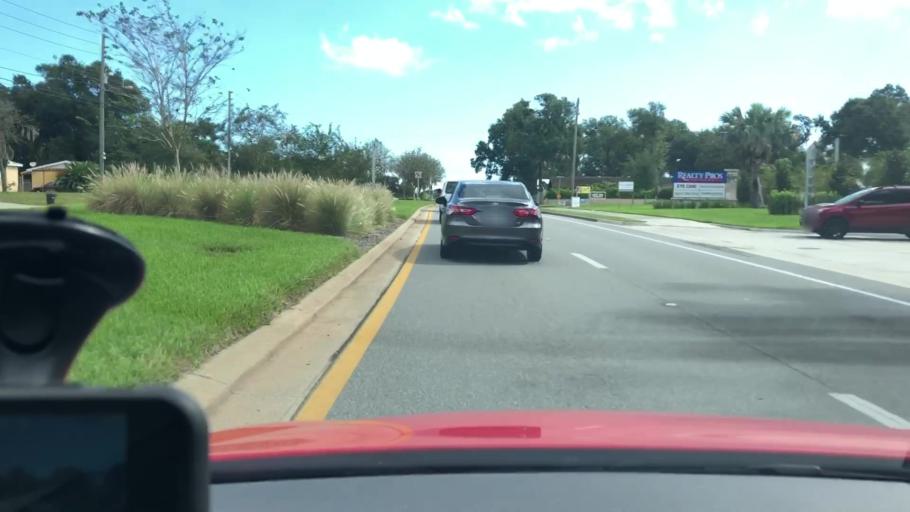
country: US
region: Florida
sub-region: Volusia County
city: Ormond Beach
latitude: 29.2782
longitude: -81.0875
